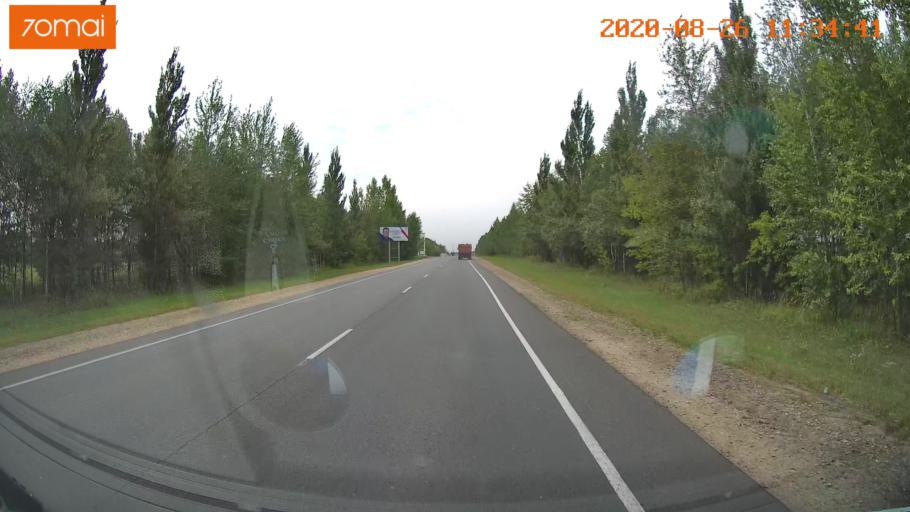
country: RU
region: Rjazan
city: Shilovo
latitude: 54.2825
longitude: 40.8409
